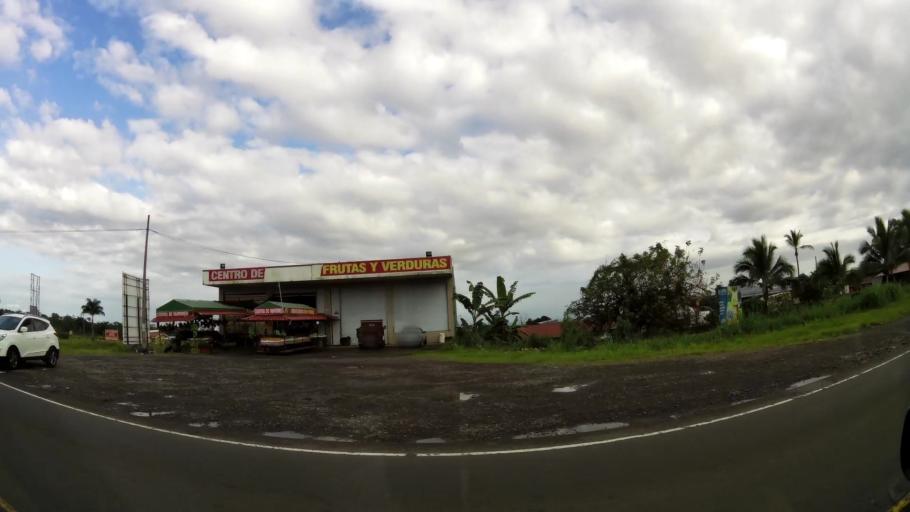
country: CR
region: Limon
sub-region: Canton de Pococi
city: Guapiles
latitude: 10.2024
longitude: -83.7993
